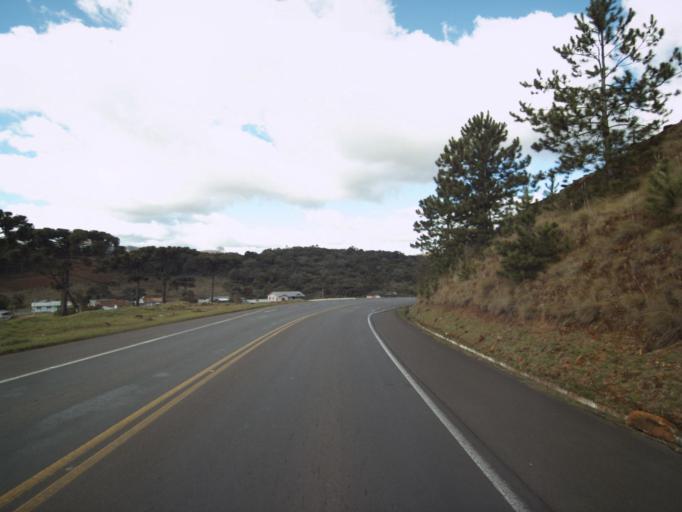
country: BR
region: Santa Catarina
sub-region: Joacaba
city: Joacaba
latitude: -27.0000
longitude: -51.7437
